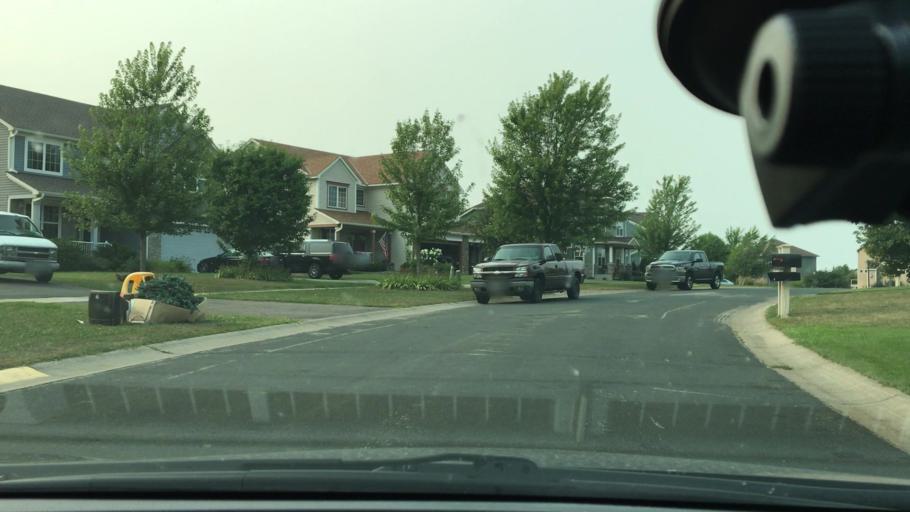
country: US
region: Minnesota
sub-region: Wright County
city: Albertville
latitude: 45.2494
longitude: -93.6447
